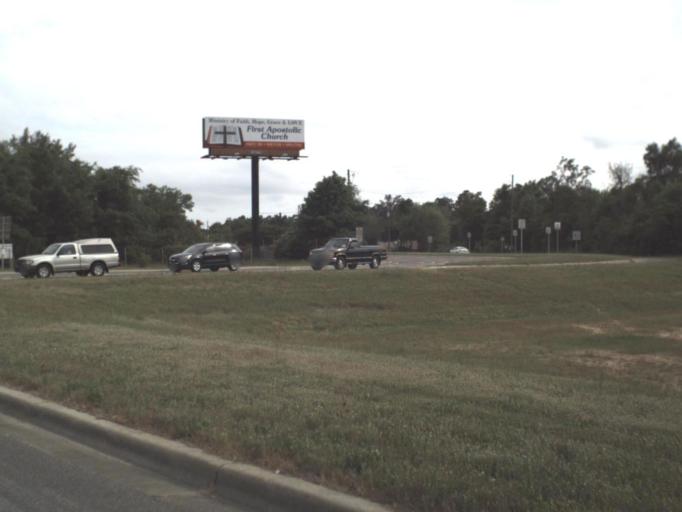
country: US
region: Florida
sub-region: Santa Rosa County
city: Point Baker
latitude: 30.6668
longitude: -87.0540
